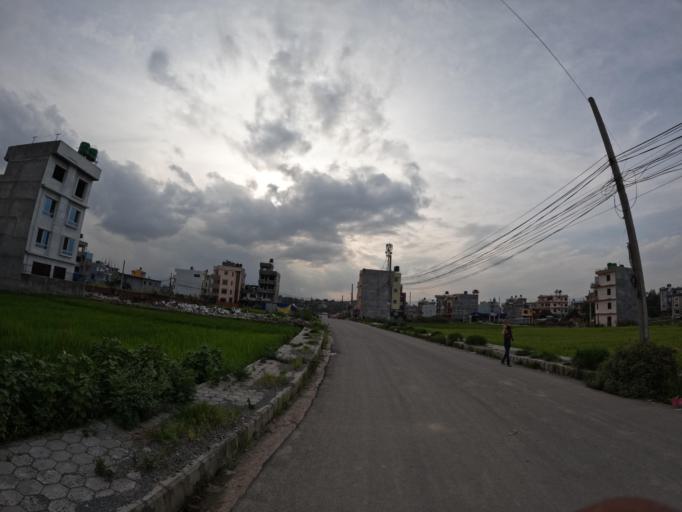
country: NP
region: Central Region
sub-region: Bagmati Zone
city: Bhaktapur
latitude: 27.6788
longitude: 85.3931
